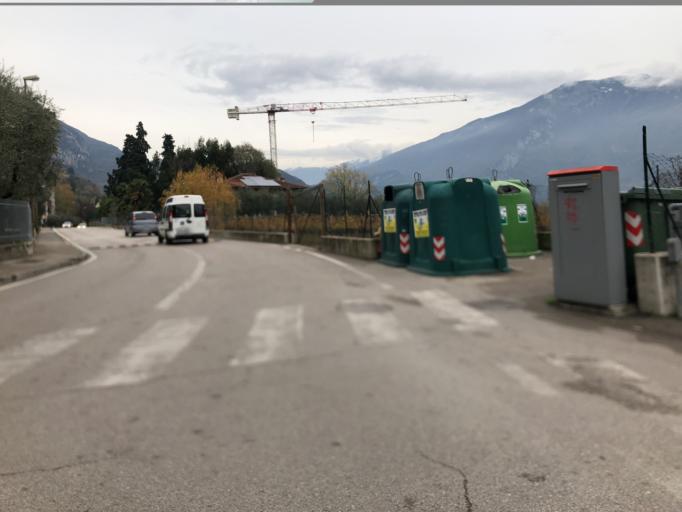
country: IT
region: Trentino-Alto Adige
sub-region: Provincia di Trento
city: Tenno
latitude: 45.9059
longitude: 10.8448
